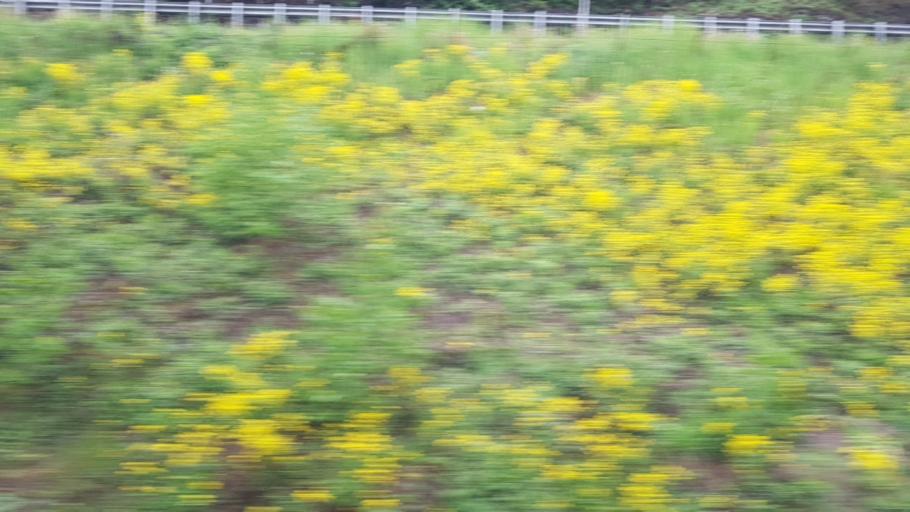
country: NO
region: Oppland
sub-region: Sor-Fron
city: Hundorp
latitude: 61.5458
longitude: 10.0232
